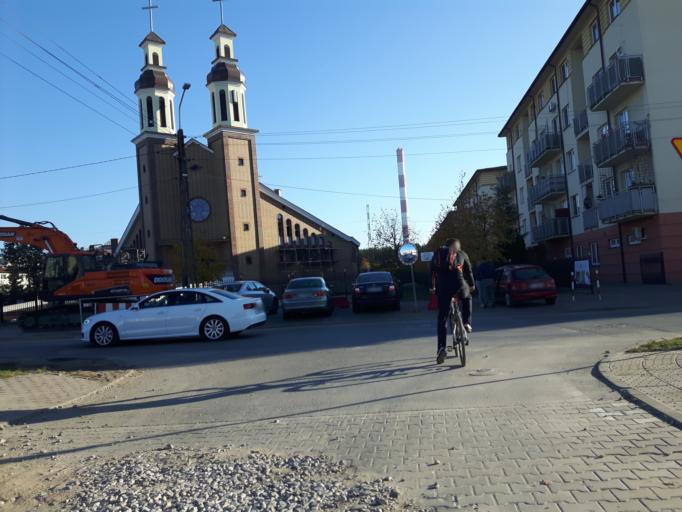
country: PL
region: Masovian Voivodeship
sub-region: Powiat wolominski
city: Zabki
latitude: 52.2794
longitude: 21.1256
